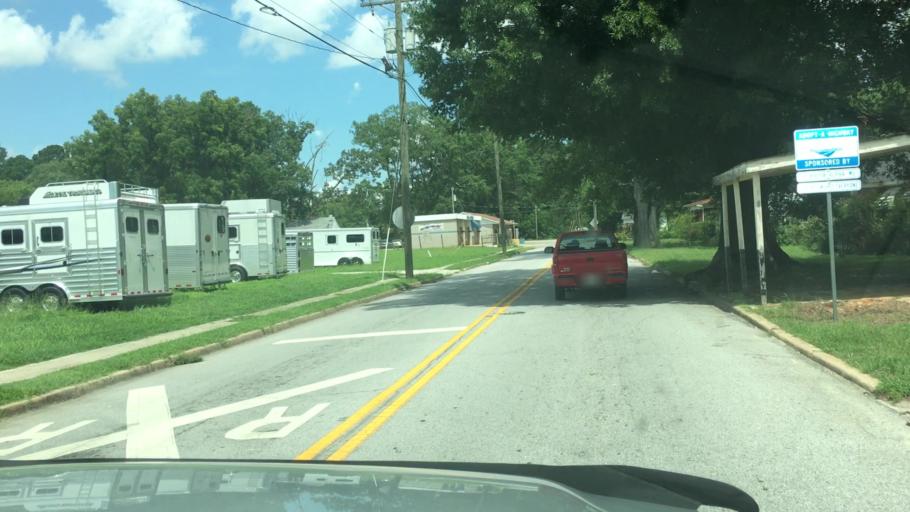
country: US
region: South Carolina
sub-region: Laurens County
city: Clinton
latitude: 34.4719
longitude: -81.8738
